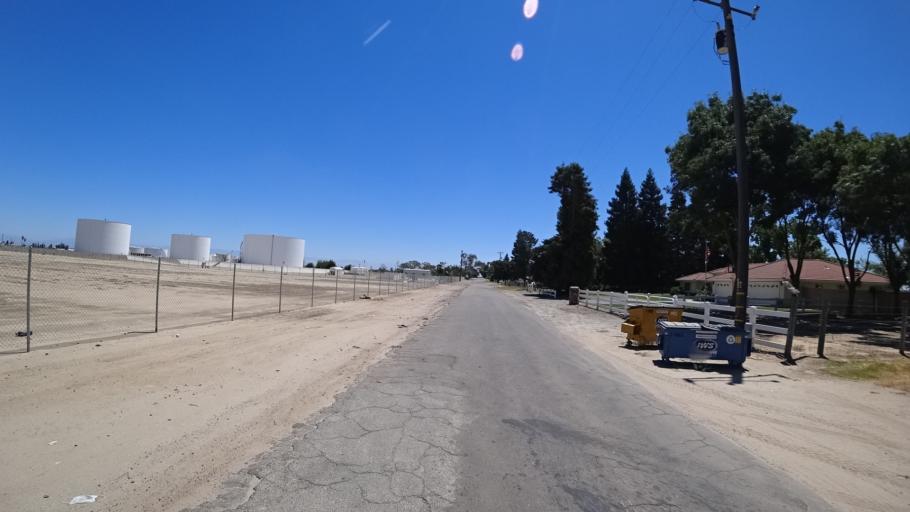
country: US
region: California
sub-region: Fresno County
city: Easton
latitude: 36.6706
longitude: -119.7540
